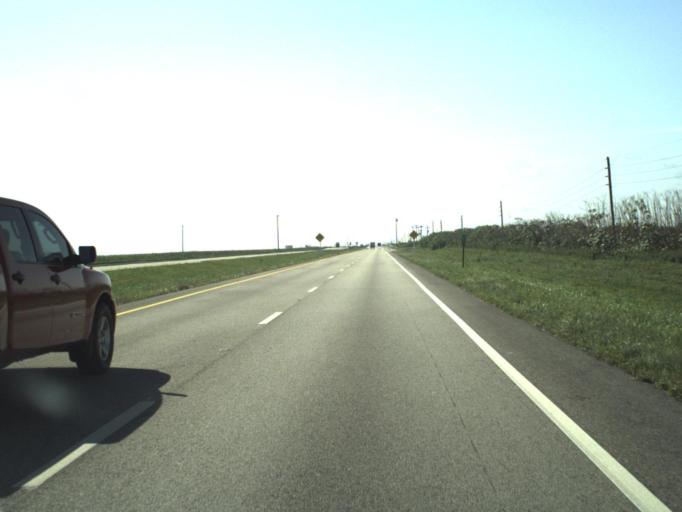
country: US
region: Florida
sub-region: Palm Beach County
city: Belle Glade Camp
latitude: 26.4022
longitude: -80.5901
